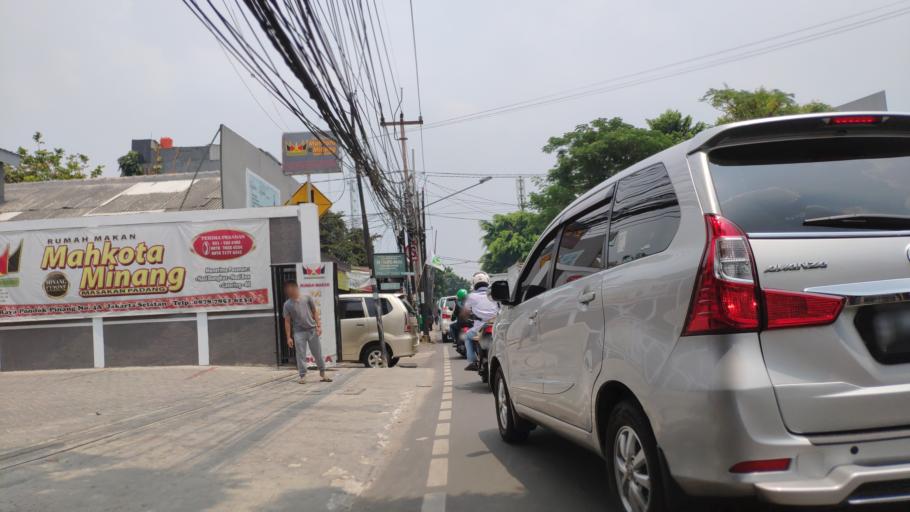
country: ID
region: Banten
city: South Tangerang
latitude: -6.2686
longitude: 106.7750
